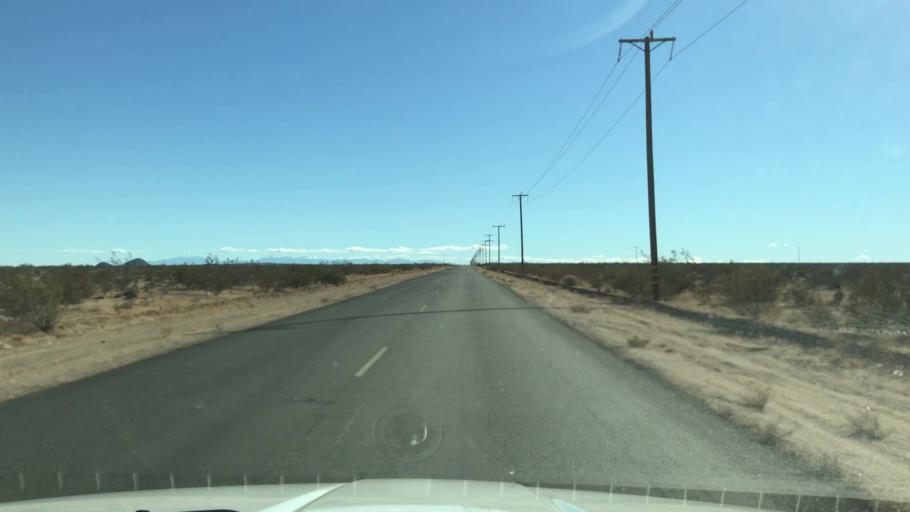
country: US
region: California
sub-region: Kern County
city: California City
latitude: 35.1892
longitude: -117.9858
